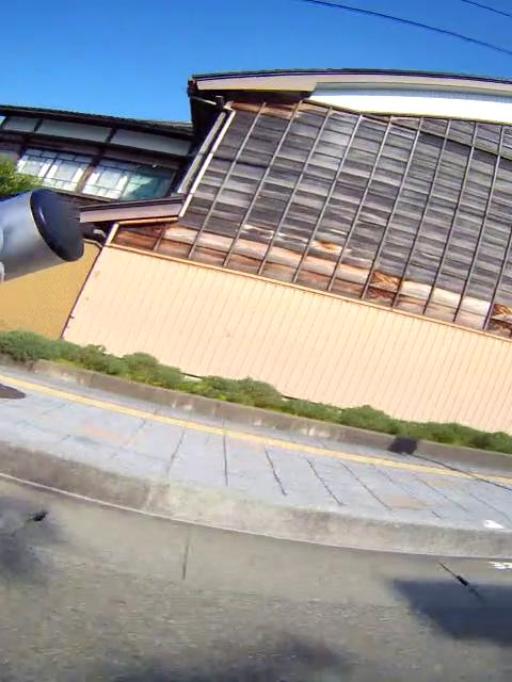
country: JP
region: Toyama
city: Fukumitsu
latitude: 36.5168
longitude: 136.9032
